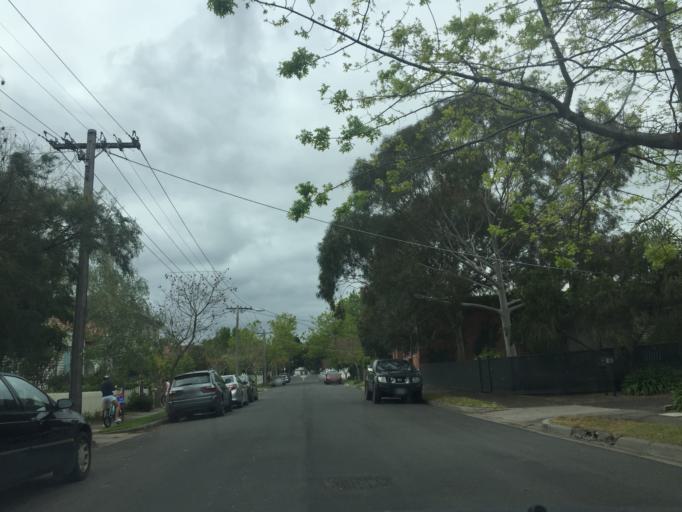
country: AU
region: Victoria
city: Balwyn
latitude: -37.8186
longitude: 145.0568
